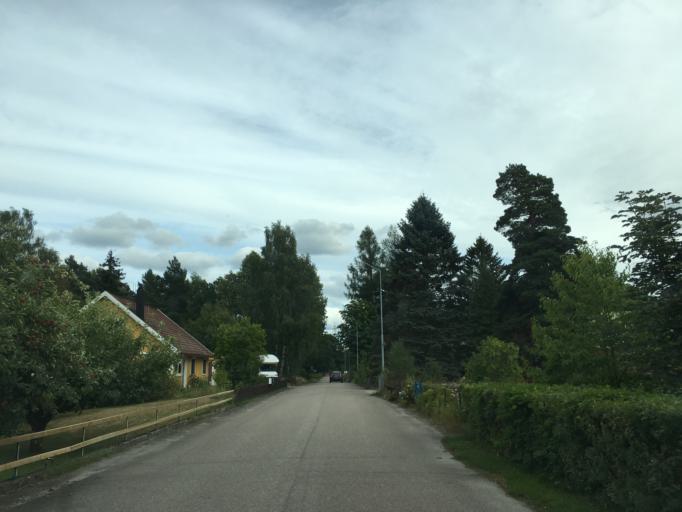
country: SE
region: Kalmar
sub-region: Nybro Kommun
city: Nybro
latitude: 56.9422
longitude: 15.9165
